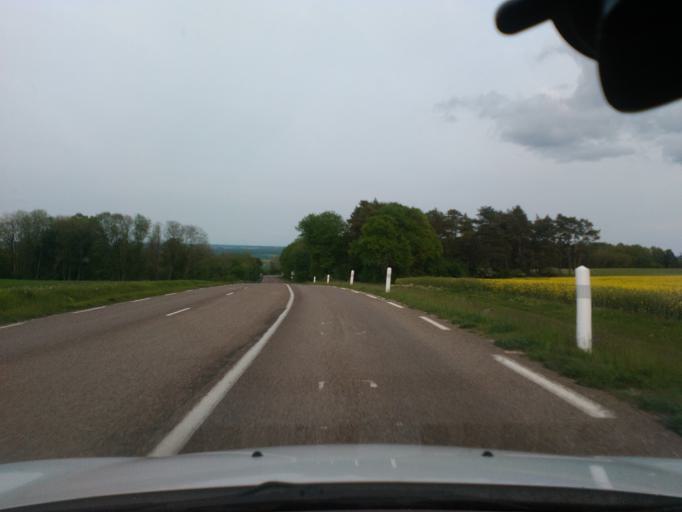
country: FR
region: Champagne-Ardenne
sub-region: Departement de la Haute-Marne
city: Chaumont
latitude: 48.1409
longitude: 5.0429
